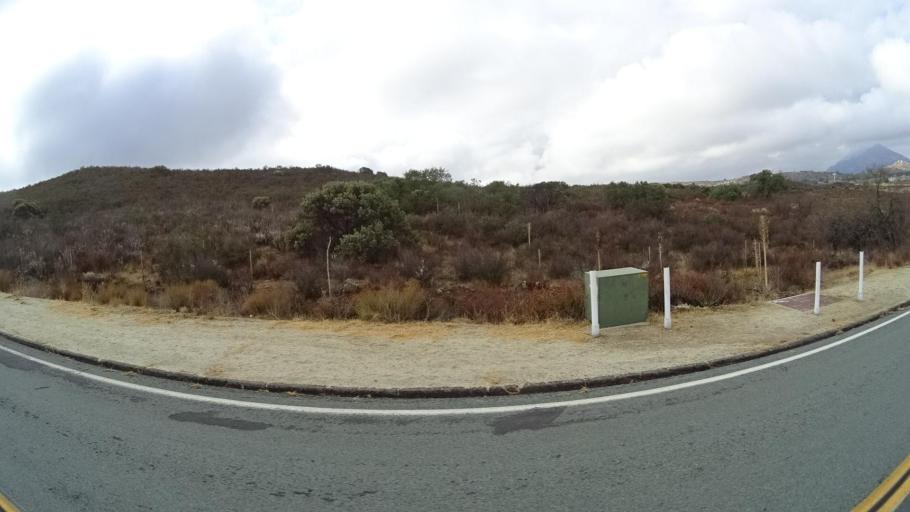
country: MX
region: Baja California
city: Tecate
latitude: 32.6152
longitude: -116.6088
